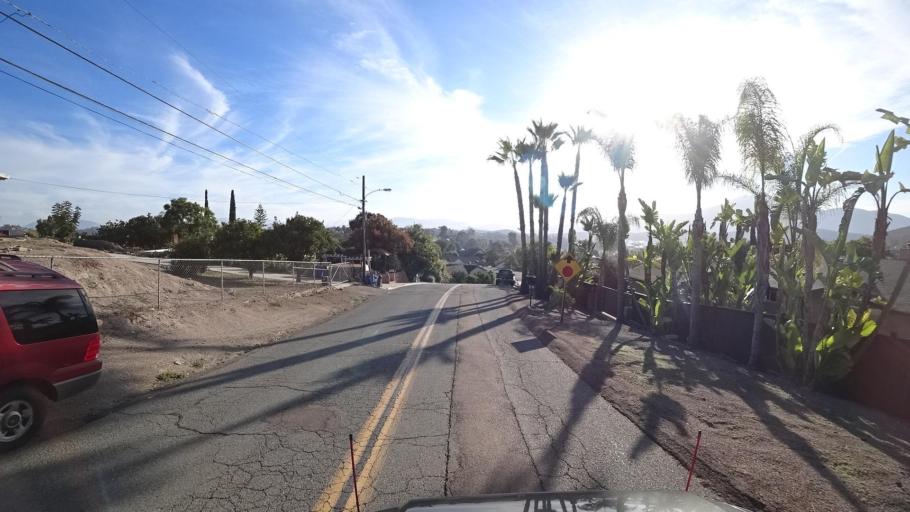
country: US
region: California
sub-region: San Diego County
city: Spring Valley
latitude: 32.7363
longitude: -116.9844
